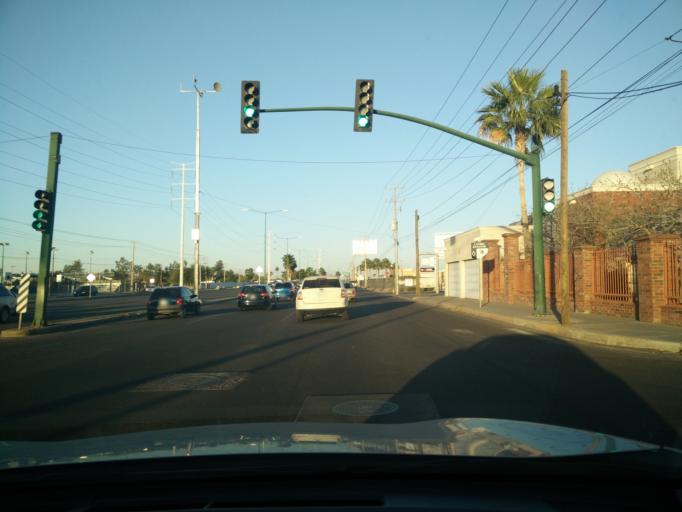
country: MX
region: Sonora
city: Hermosillo
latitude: 29.0836
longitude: -111.0010
